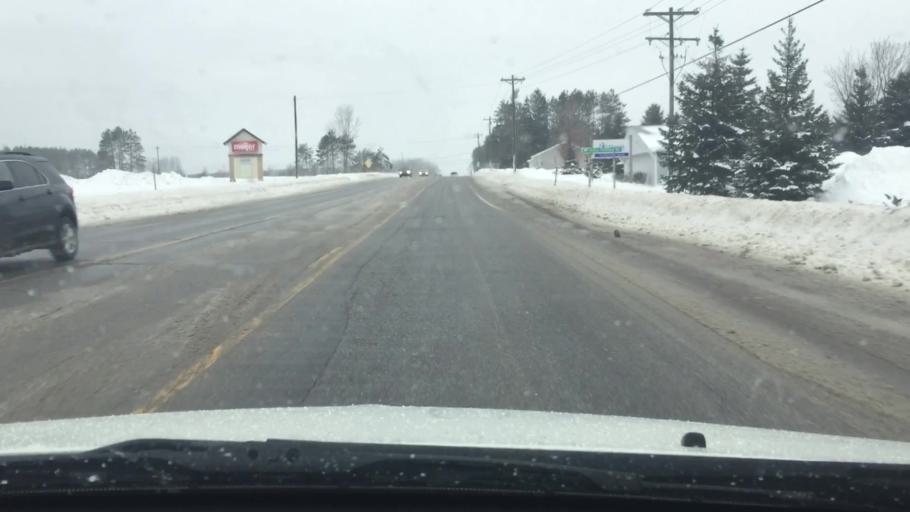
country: US
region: Michigan
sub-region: Otsego County
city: Gaylord
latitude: 45.0279
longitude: -84.7244
